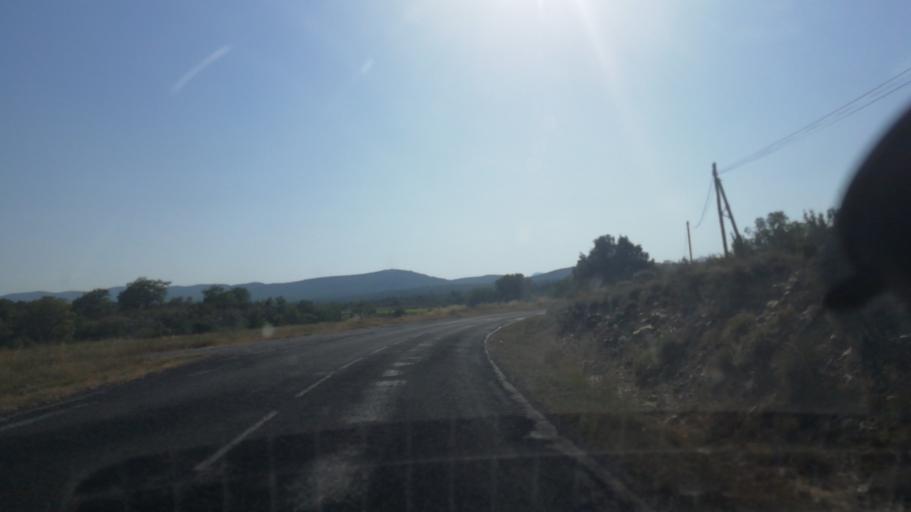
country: FR
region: Languedoc-Roussillon
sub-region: Departement de l'Herault
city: Saint-Martin-de-Londres
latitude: 43.8231
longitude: 3.7708
